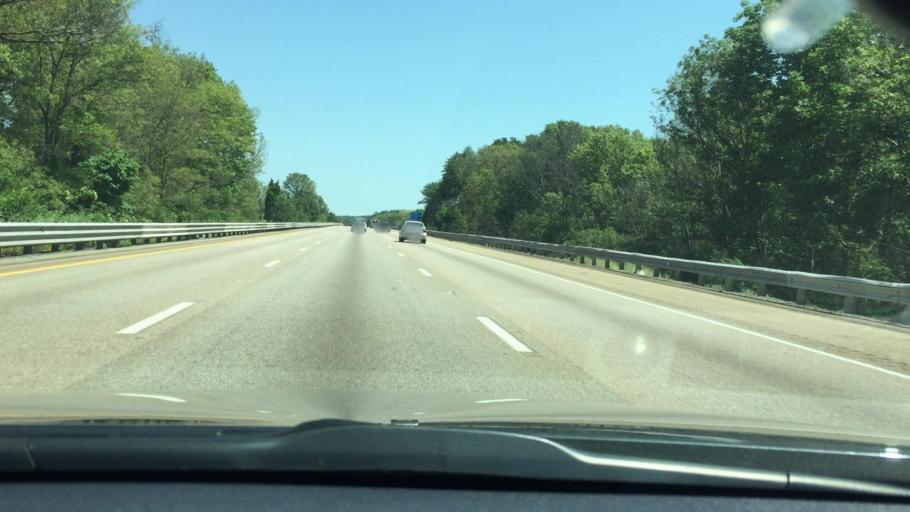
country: US
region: Massachusetts
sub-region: Norfolk County
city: Canton
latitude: 42.1849
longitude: -71.1579
